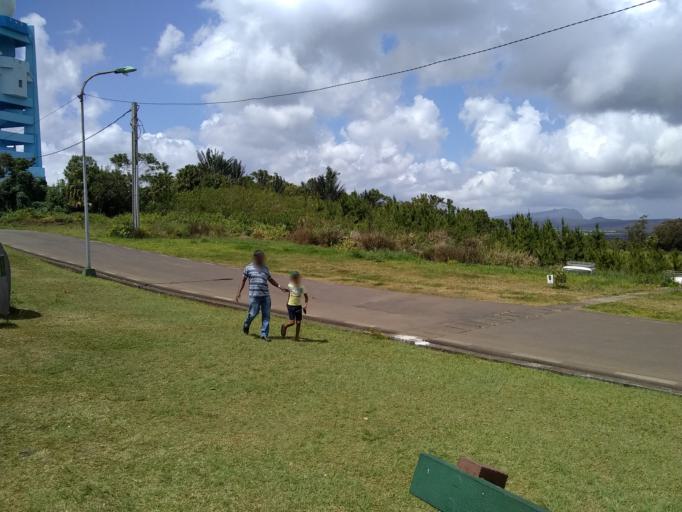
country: MU
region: Plaines Wilhems
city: Curepipe
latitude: -20.3177
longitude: 57.5098
